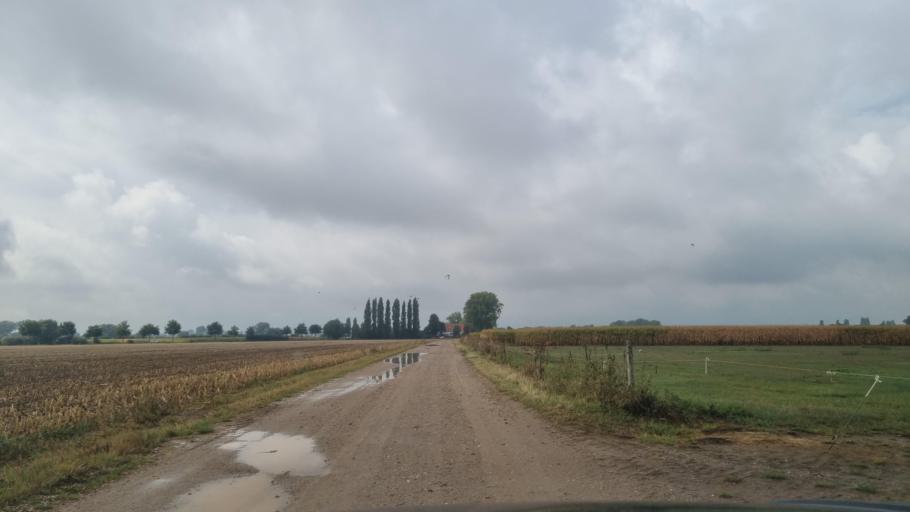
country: DE
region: North Rhine-Westphalia
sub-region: Regierungsbezirk Dusseldorf
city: Kranenburg
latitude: 51.8499
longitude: 6.0488
